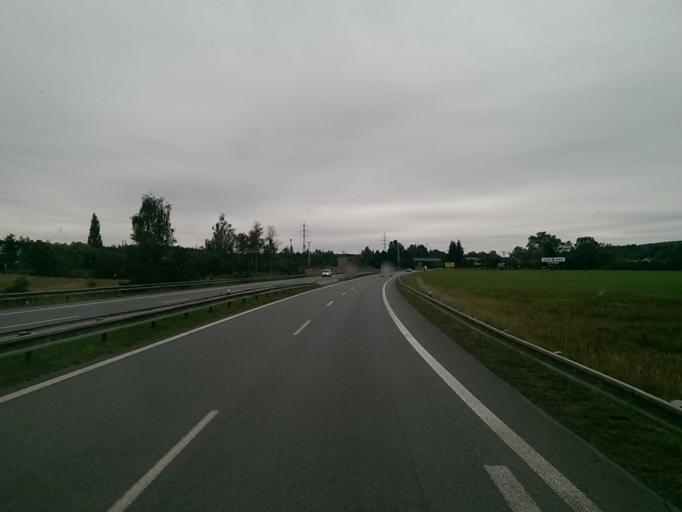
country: CZ
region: Vysocina
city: Dobronin
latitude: 49.4471
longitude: 15.6104
